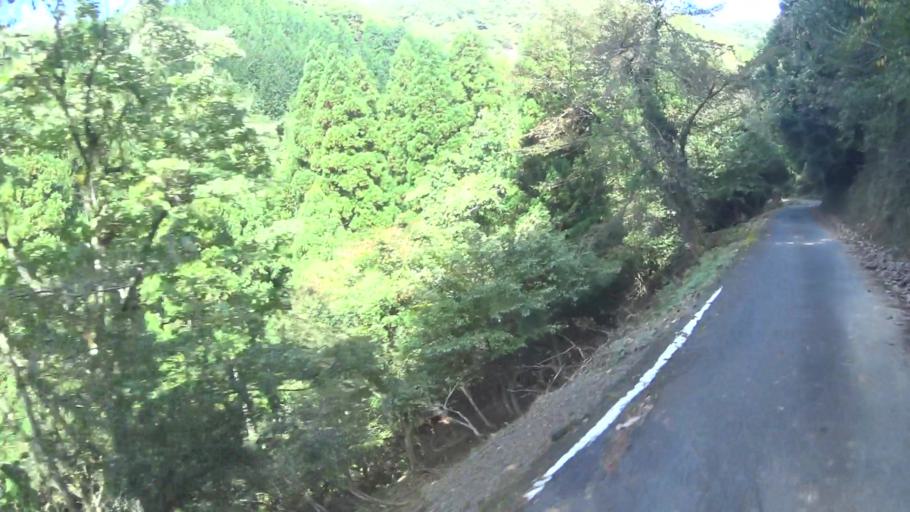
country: JP
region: Hyogo
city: Toyooka
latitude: 35.6119
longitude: 134.9927
